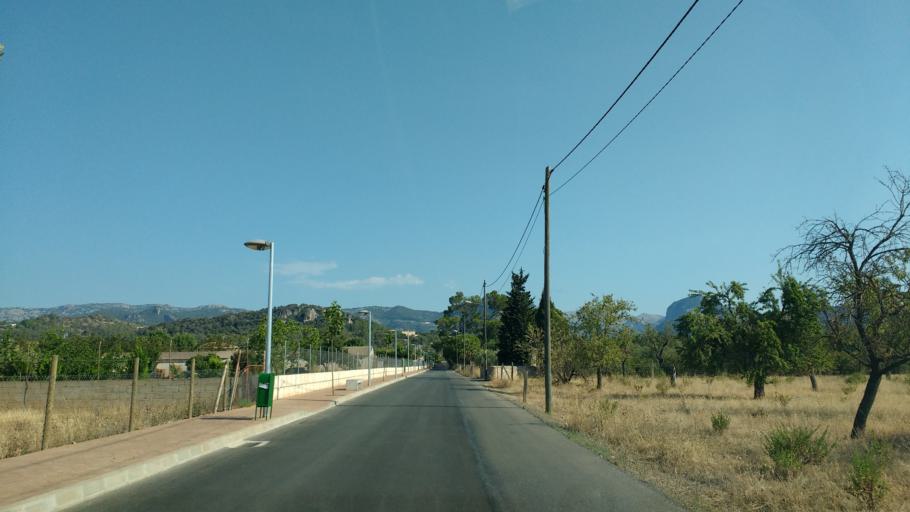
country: ES
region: Balearic Islands
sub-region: Illes Balears
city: Consell
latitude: 39.6758
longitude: 2.8102
